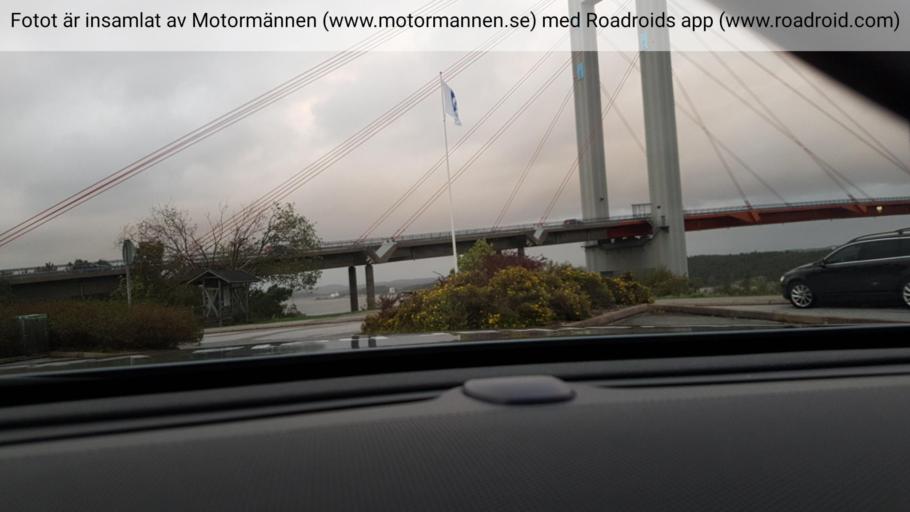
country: SE
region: Vaestra Goetaland
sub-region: Tjorns Kommun
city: Myggenas
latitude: 58.0587
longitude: 11.7759
